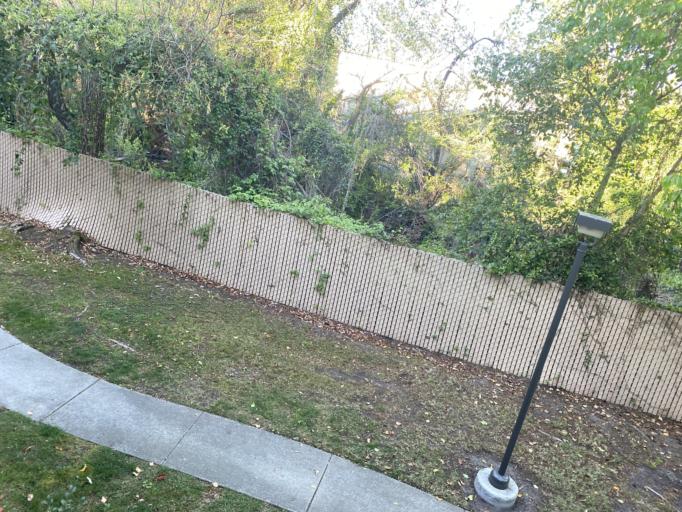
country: US
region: California
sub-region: Santa Clara County
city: Milpitas
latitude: 37.4945
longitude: -121.9272
